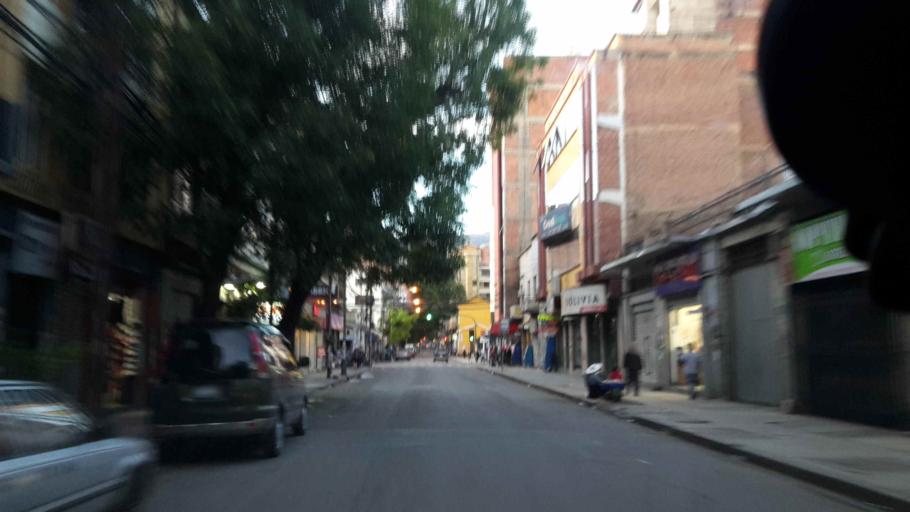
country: BO
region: Cochabamba
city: Cochabamba
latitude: -17.3958
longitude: -66.1541
